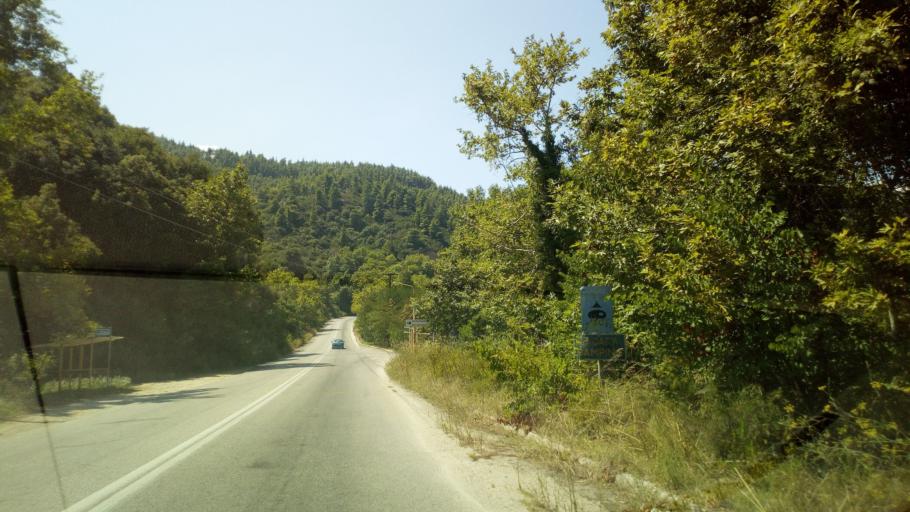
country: GR
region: Central Macedonia
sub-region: Nomos Chalkidikis
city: Neos Marmaras
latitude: 40.1703
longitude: 23.8554
